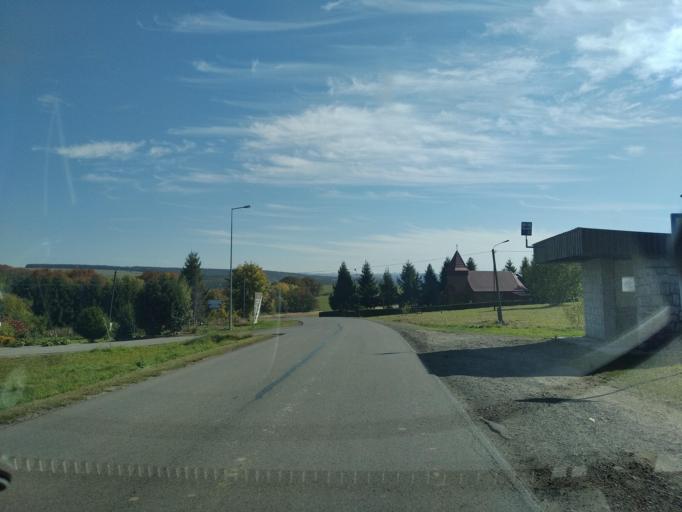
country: PL
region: Subcarpathian Voivodeship
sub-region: Powiat sanocki
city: Komancza
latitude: 49.3679
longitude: 22.0052
